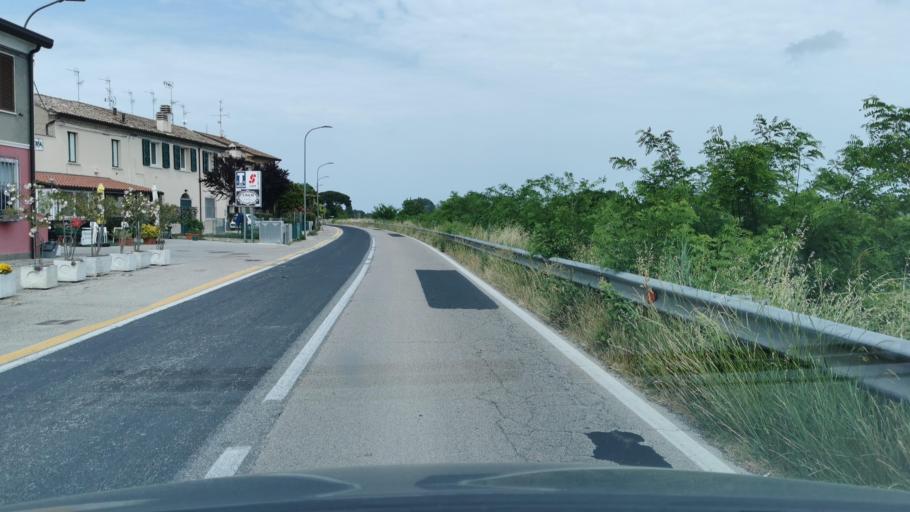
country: IT
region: Emilia-Romagna
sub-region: Provincia di Ravenna
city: Marina Romea
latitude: 44.5526
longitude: 12.2248
